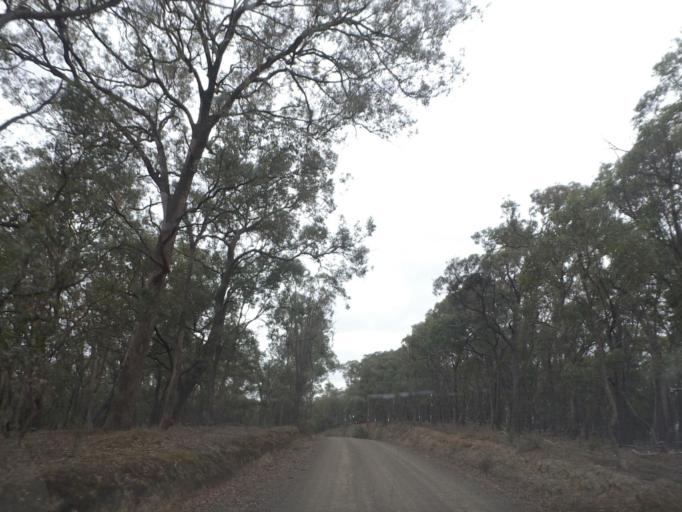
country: AU
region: Victoria
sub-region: Yarra Ranges
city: Yarra Glen
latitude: -37.6782
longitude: 145.3308
